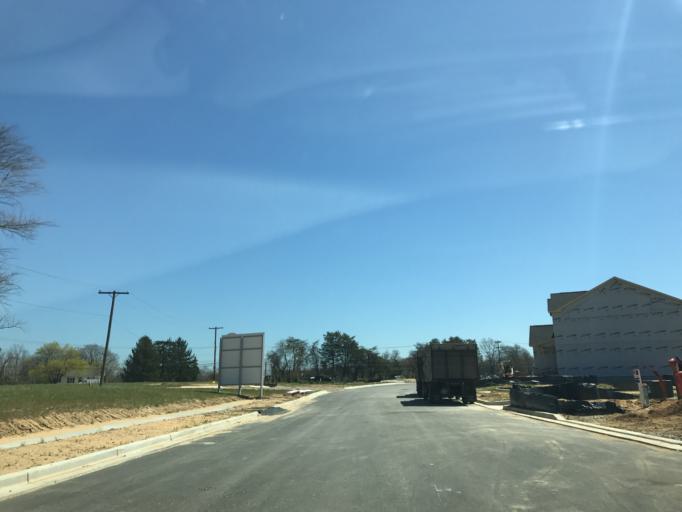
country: US
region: Maryland
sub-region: Anne Arundel County
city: Fort Meade
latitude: 39.1350
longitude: -76.7365
